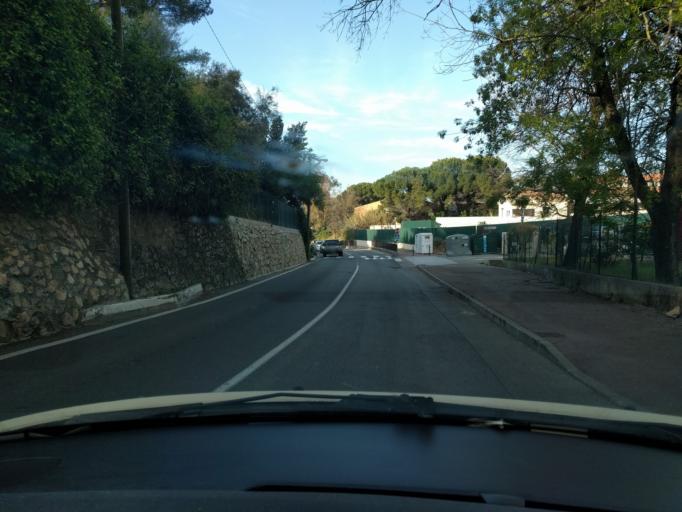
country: FR
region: Provence-Alpes-Cote d'Azur
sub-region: Departement des Alpes-Maritimes
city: Mougins
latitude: 43.5880
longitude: 6.9991
